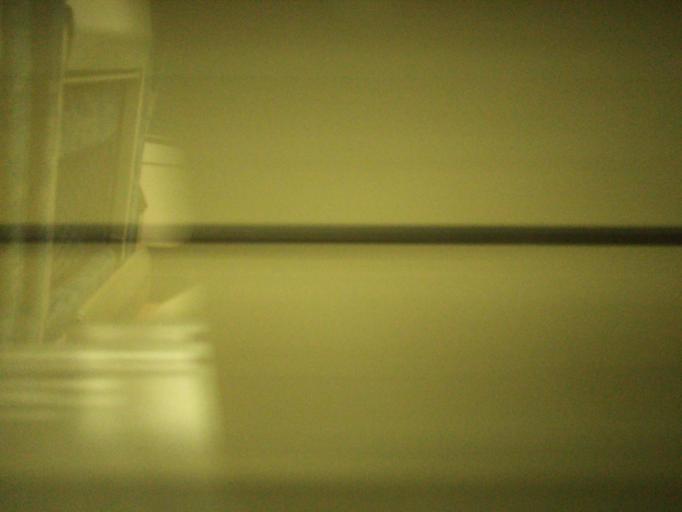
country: JP
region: Kochi
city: Nakamura
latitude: 33.0664
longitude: 133.1069
